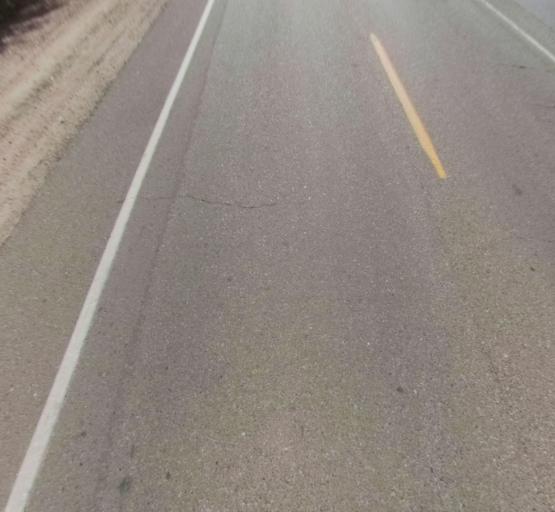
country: US
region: California
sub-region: Madera County
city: Chowchilla
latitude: 37.1127
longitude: -120.3376
